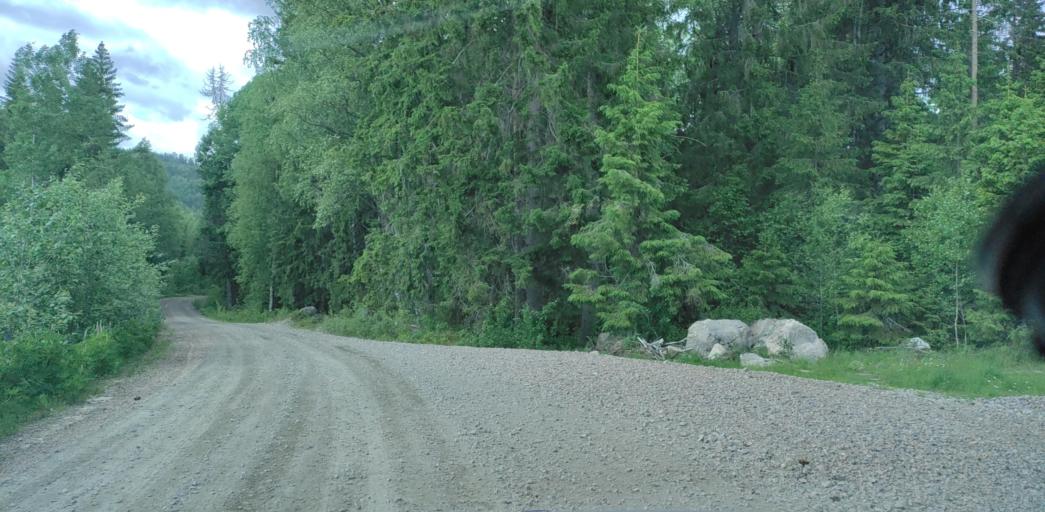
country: SE
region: Vaermland
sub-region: Munkfors Kommun
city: Munkfors
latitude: 59.9681
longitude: 13.4246
